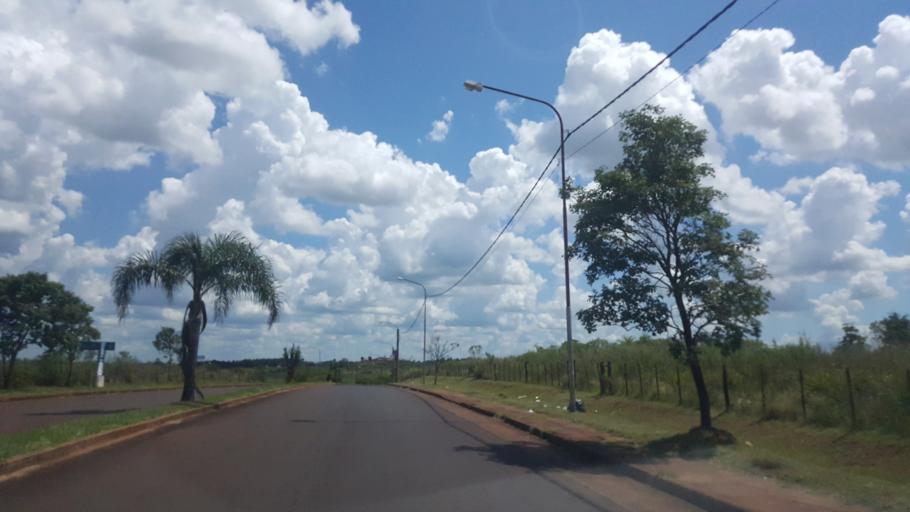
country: AR
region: Misiones
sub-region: Departamento de Capital
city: Posadas
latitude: -27.3802
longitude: -55.9626
